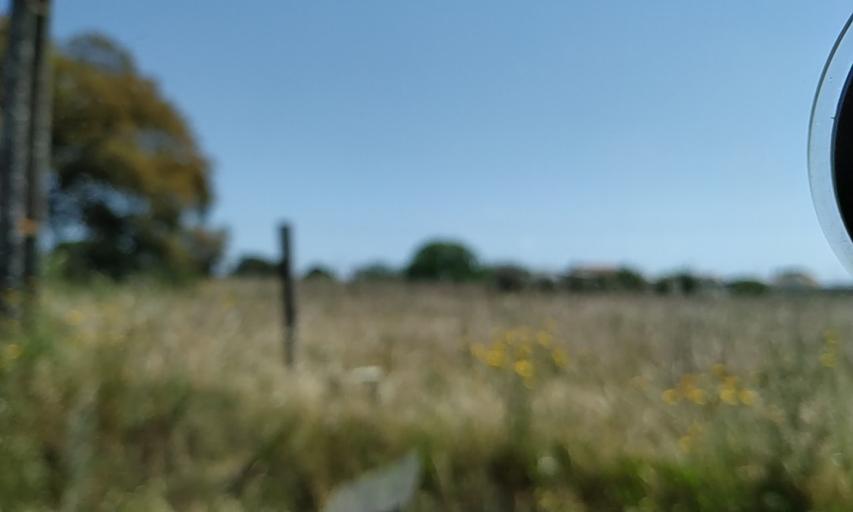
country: PT
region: Setubal
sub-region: Palmela
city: Palmela
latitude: 38.6160
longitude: -8.7567
